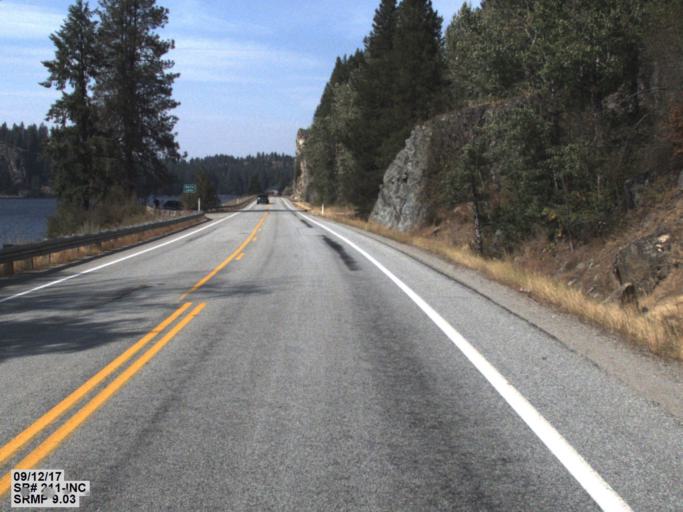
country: US
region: Washington
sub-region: Pend Oreille County
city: Newport
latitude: 48.2178
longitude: -117.2910
